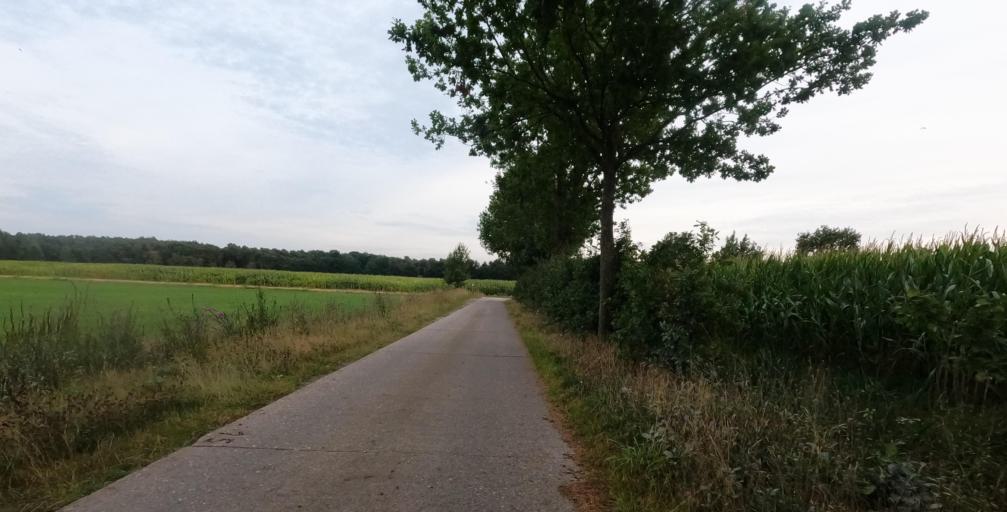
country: BE
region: Flanders
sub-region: Provincie Antwerpen
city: Essen
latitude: 51.4612
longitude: 4.5140
